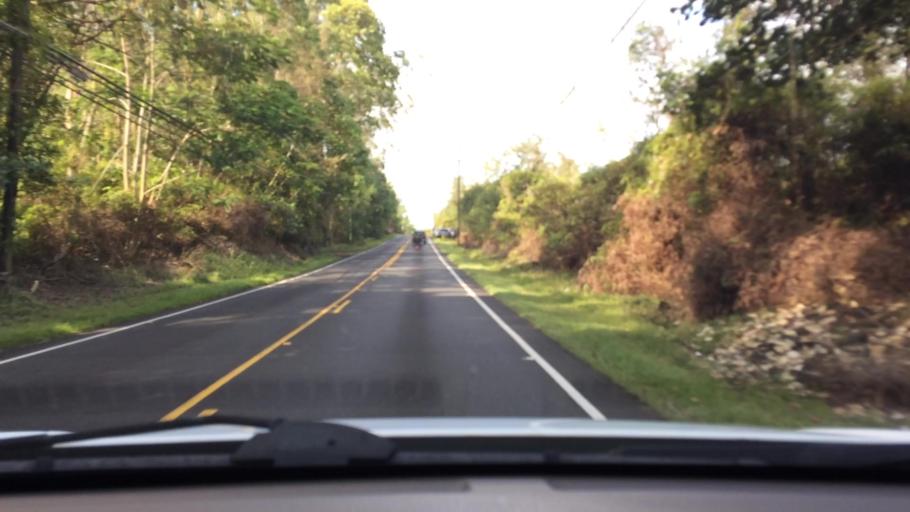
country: US
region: Hawaii
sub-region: Hawaii County
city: Hawaiian Paradise Park
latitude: 19.5064
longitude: -154.9497
